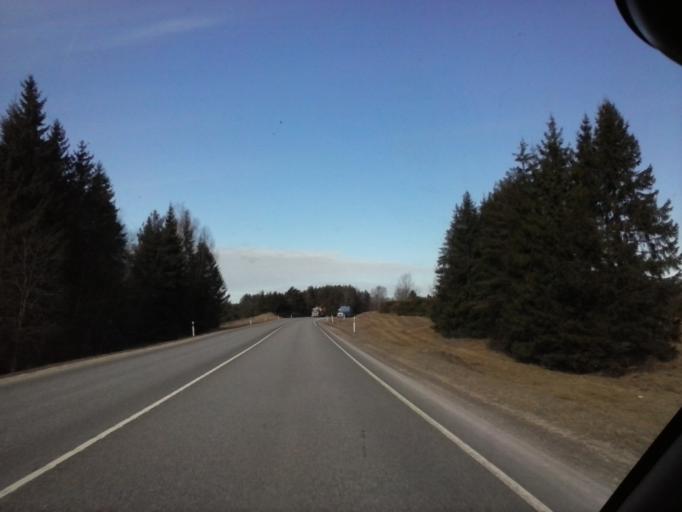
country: EE
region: Harju
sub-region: Anija vald
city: Kehra
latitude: 59.1030
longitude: 25.3351
